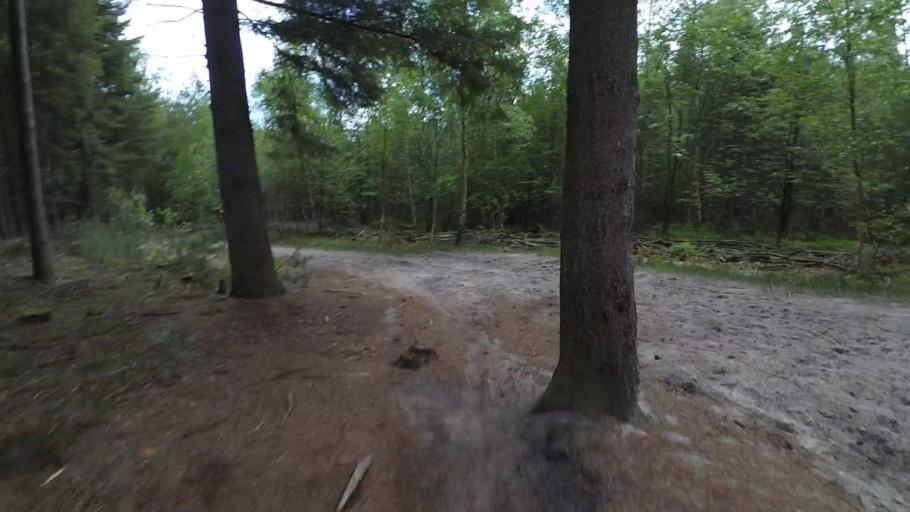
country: NL
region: Utrecht
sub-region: Gemeente Utrechtse Heuvelrug
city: Maarn
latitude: 52.0901
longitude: 5.3552
